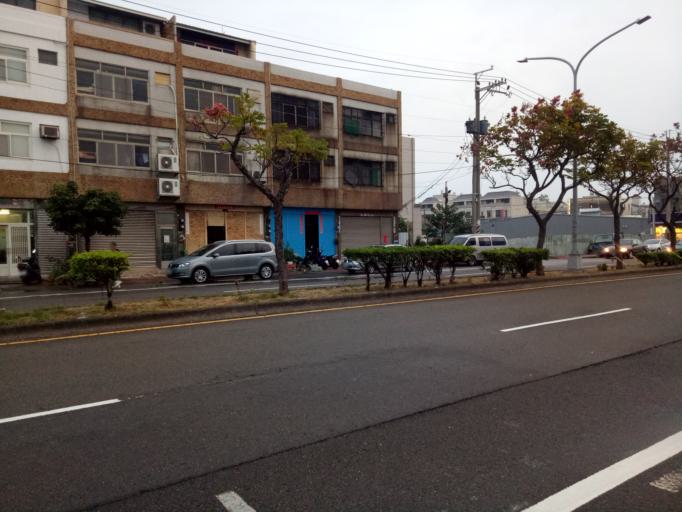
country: TW
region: Taiwan
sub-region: Changhua
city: Chang-hua
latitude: 24.2451
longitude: 120.5387
